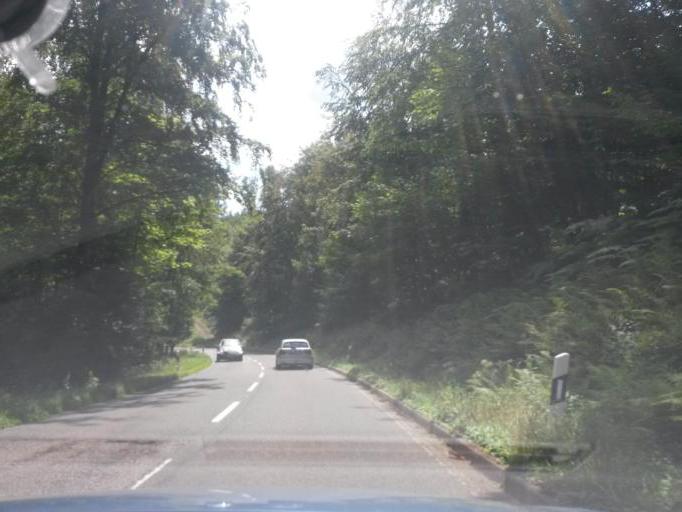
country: DE
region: Baden-Wuerttemberg
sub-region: Karlsruhe Region
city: Bad Herrenalb
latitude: 48.8647
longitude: 8.4435
